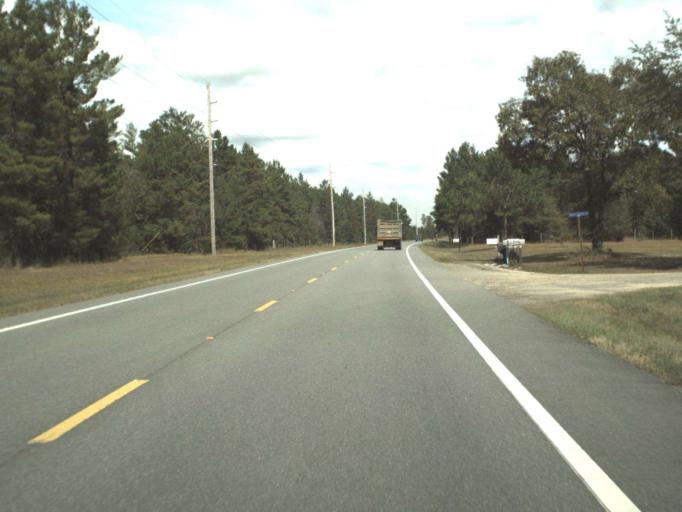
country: US
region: Florida
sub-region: Gadsden County
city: Quincy
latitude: 30.4336
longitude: -84.6480
